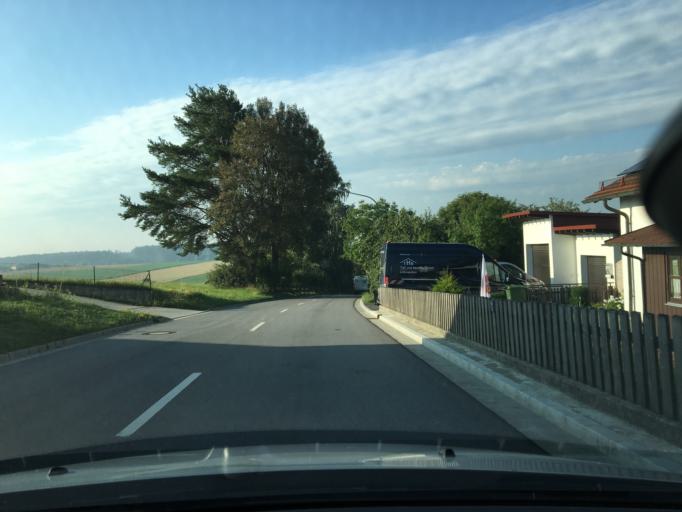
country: DE
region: Bavaria
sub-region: Lower Bavaria
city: Vilsbiburg
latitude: 48.4799
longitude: 12.3411
